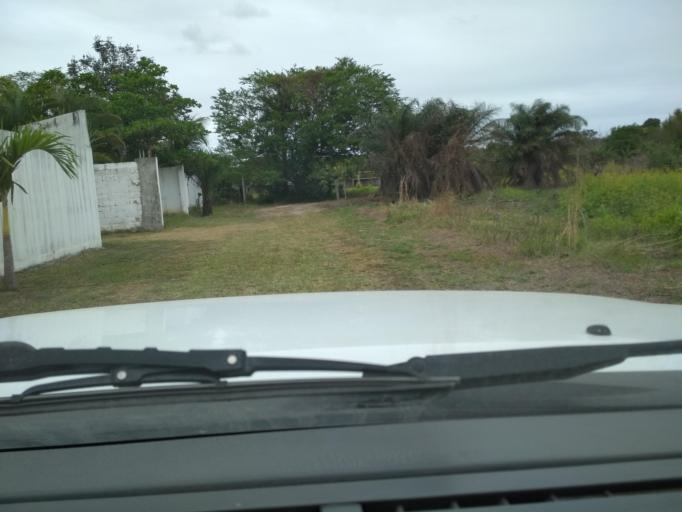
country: MX
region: Veracruz
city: Paso del Toro
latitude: 19.0533
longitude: -96.1384
